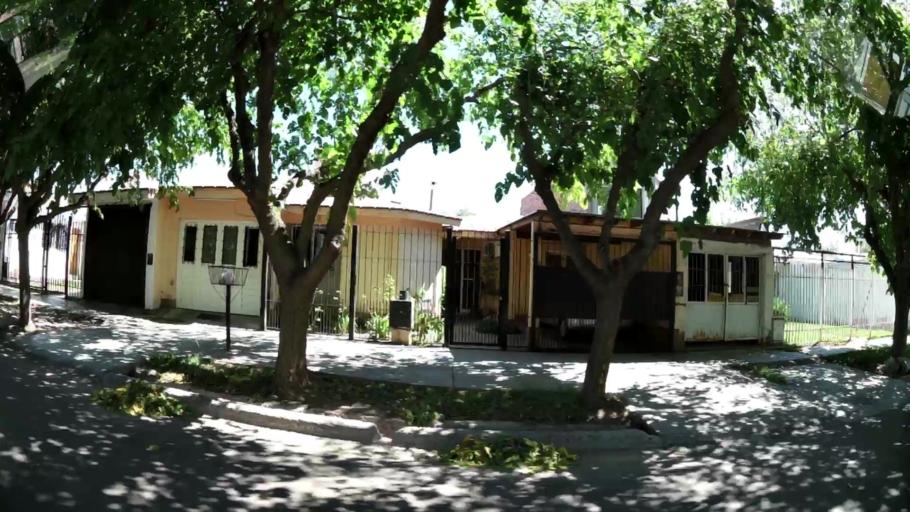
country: AR
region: Mendoza
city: Las Heras
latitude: -32.8509
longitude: -68.8507
